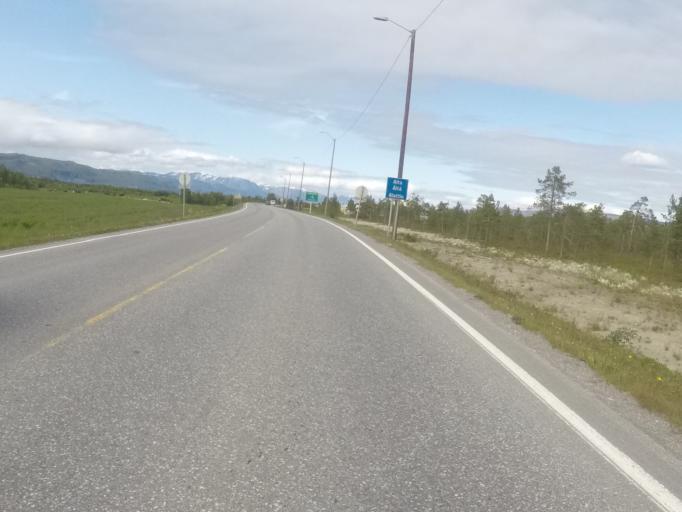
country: NO
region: Finnmark Fylke
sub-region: Alta
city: Alta
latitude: 69.9472
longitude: 23.2408
